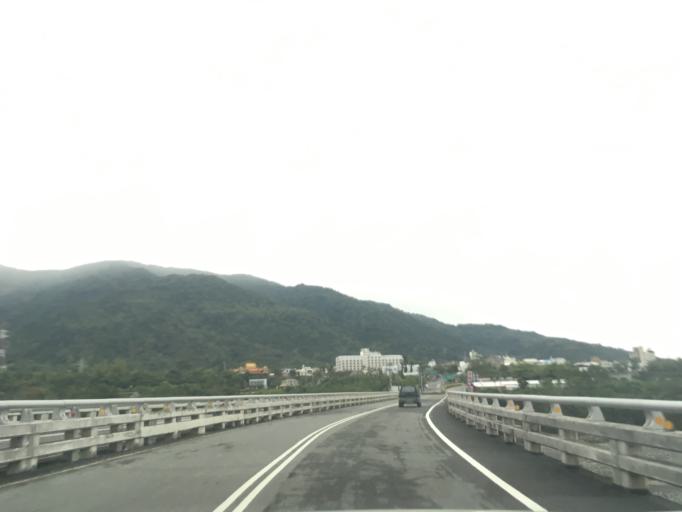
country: TW
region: Taiwan
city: Taitung City
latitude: 22.7002
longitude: 121.0398
